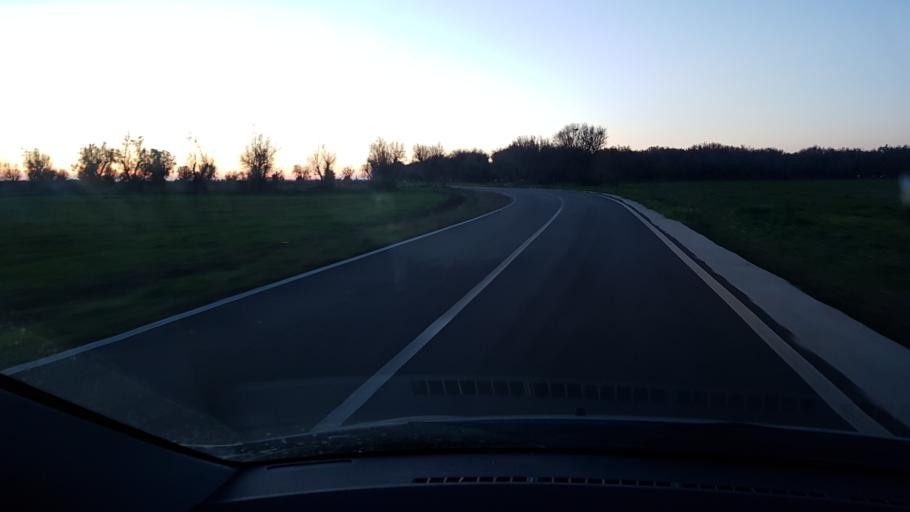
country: IT
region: Apulia
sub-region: Provincia di Brindisi
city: Tuturano
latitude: 40.5269
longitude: 17.9111
